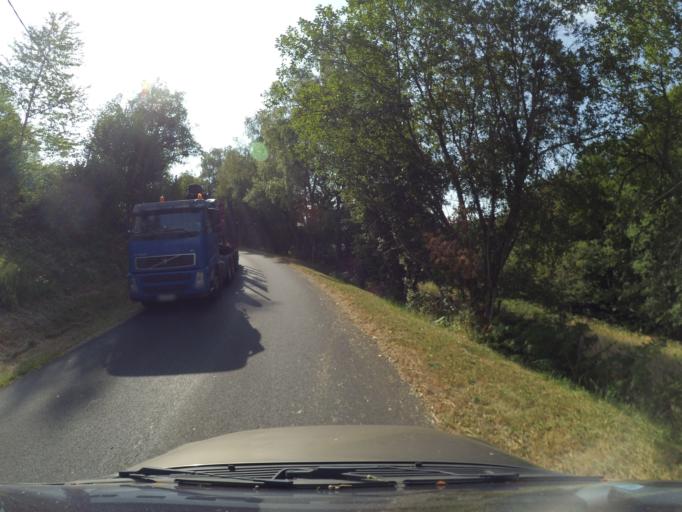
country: FR
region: Limousin
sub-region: Departement de la Correze
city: Bugeat
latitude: 45.6983
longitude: 2.0561
